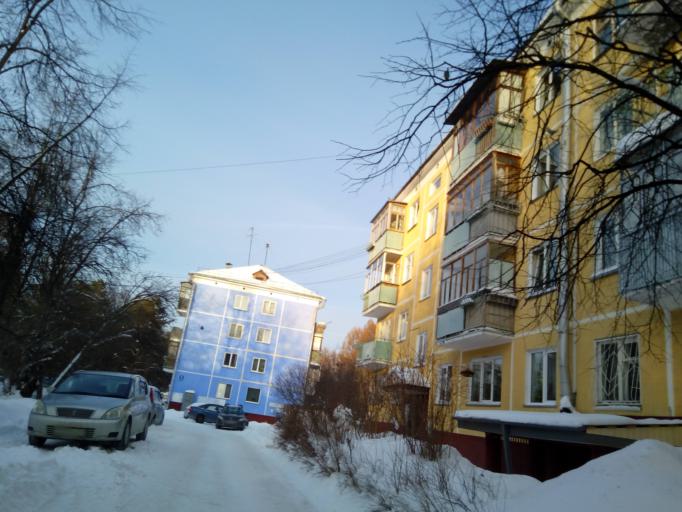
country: RU
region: Novosibirsk
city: Akademgorodok
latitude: 54.8363
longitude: 83.1071
